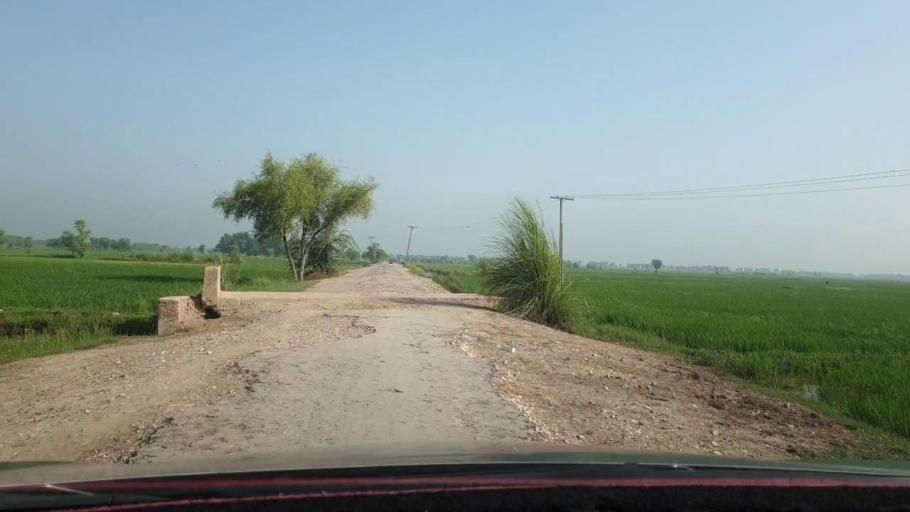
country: PK
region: Sindh
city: Nasirabad
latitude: 27.4374
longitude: 67.9205
